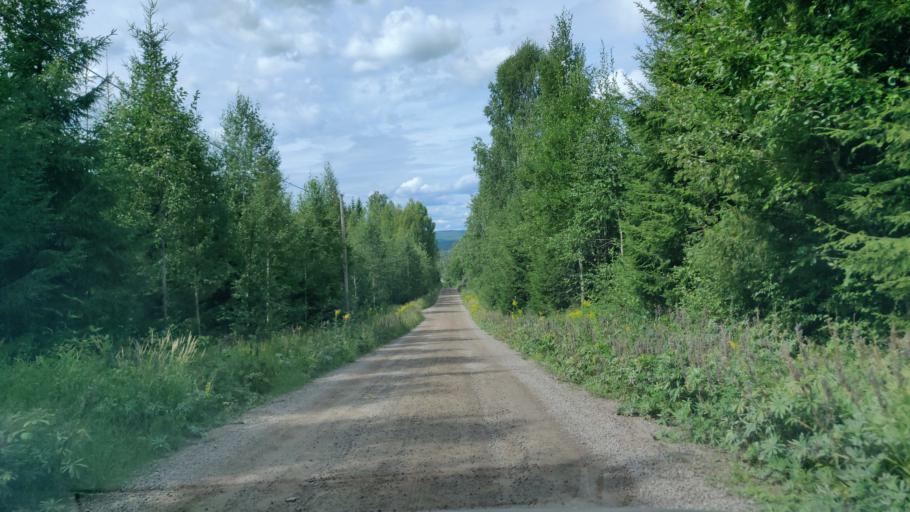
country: SE
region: Vaermland
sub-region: Hagfors Kommun
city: Hagfors
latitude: 60.0180
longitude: 13.7019
